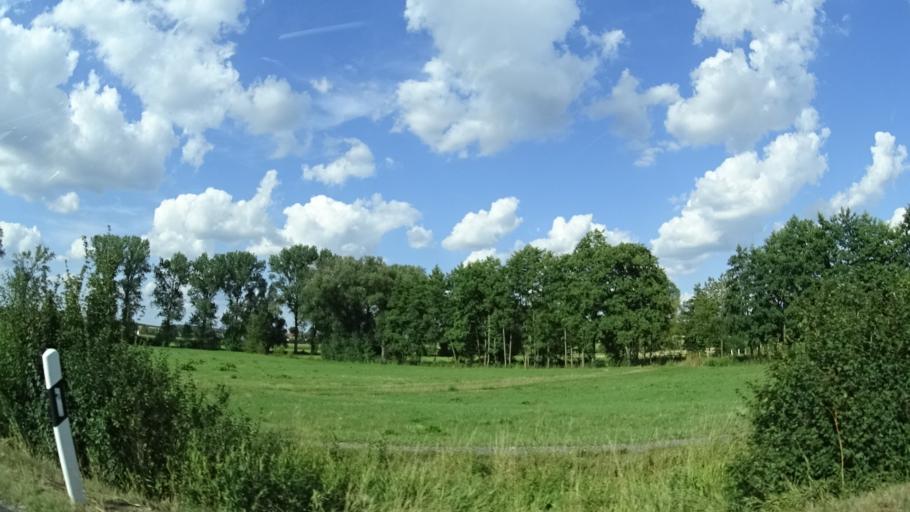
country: DE
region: Bavaria
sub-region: Regierungsbezirk Unterfranken
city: Bad Konigshofen im Grabfeld
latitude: 50.2934
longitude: 10.4851
